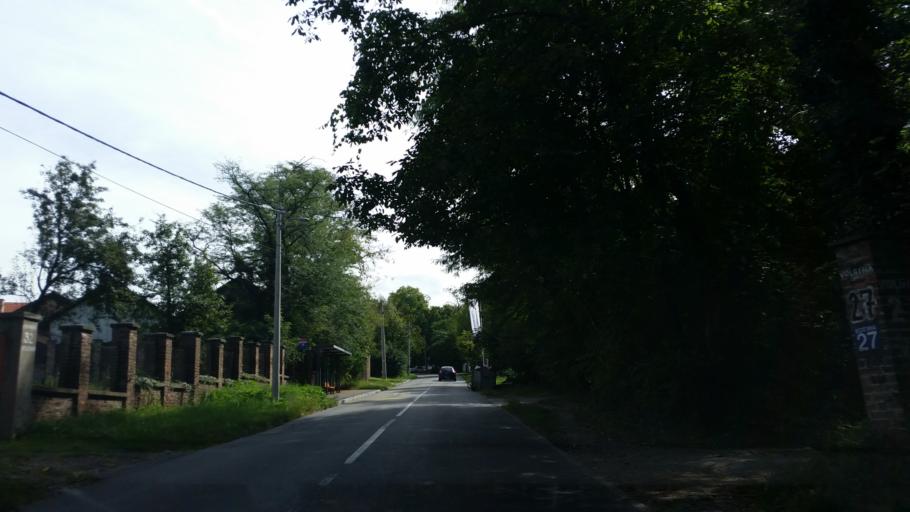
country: RS
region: Central Serbia
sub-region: Belgrade
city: Palilula
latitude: 44.8088
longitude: 20.5026
